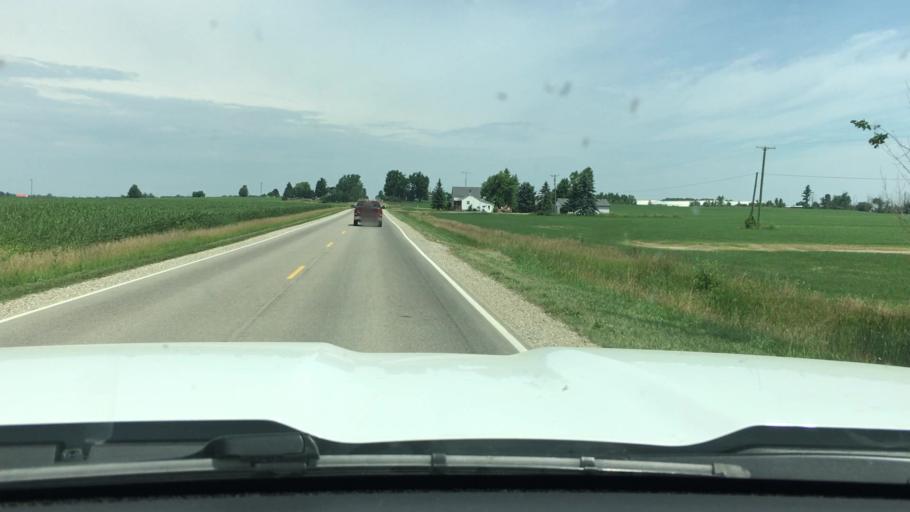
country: US
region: Michigan
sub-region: Sanilac County
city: Brown City
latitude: 43.3034
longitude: -82.9834
